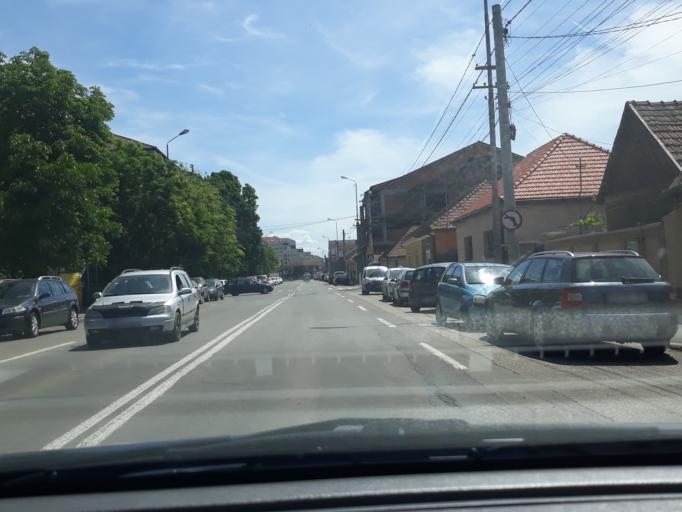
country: RO
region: Bihor
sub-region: Comuna Biharea
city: Oradea
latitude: 47.0657
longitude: 21.9016
